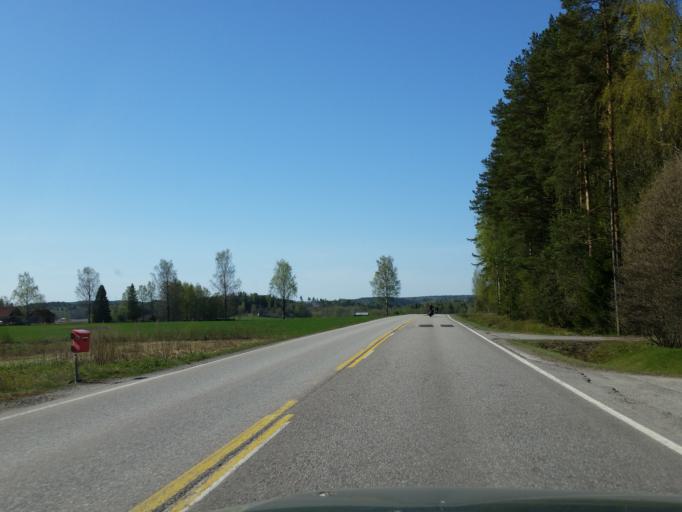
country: FI
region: Uusimaa
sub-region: Helsinki
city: Siuntio
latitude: 60.1878
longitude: 24.2447
